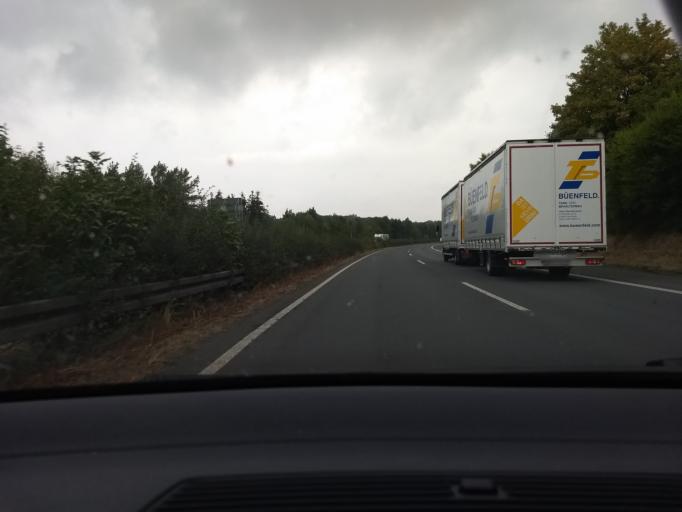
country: DE
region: North Rhine-Westphalia
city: Wickede
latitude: 51.4440
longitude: 7.9582
